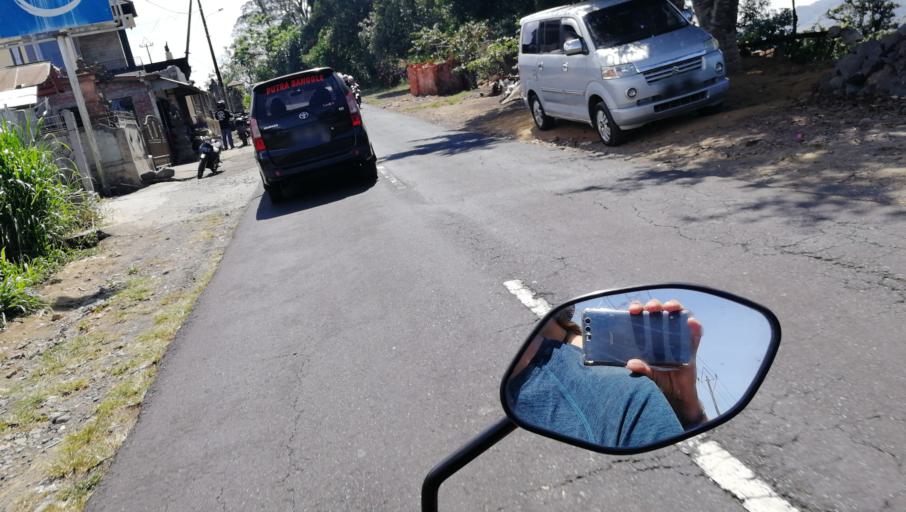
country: ID
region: Bali
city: Munduk
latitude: -8.2388
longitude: 115.1108
